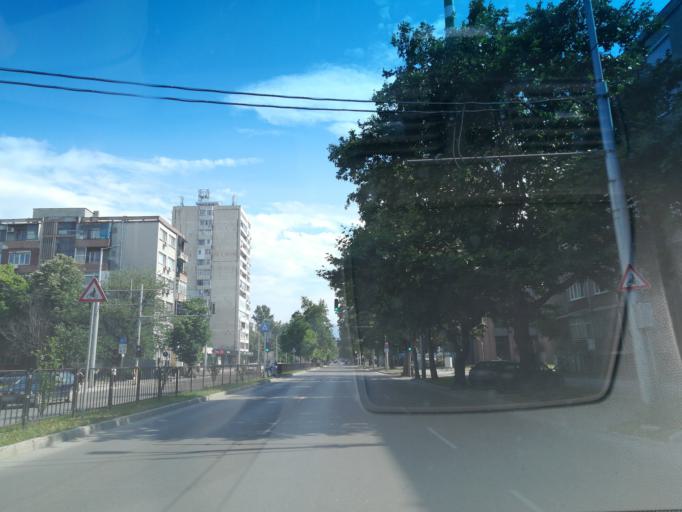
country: BG
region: Plovdiv
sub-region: Obshtina Plovdiv
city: Plovdiv
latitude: 42.1445
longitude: 24.7631
